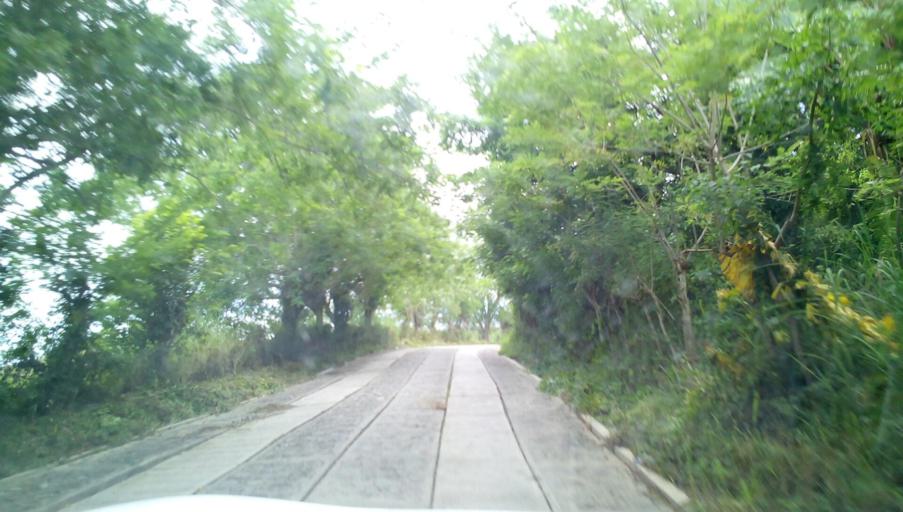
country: MX
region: Veracruz
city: Tepetzintla
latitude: 21.1576
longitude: -97.8524
